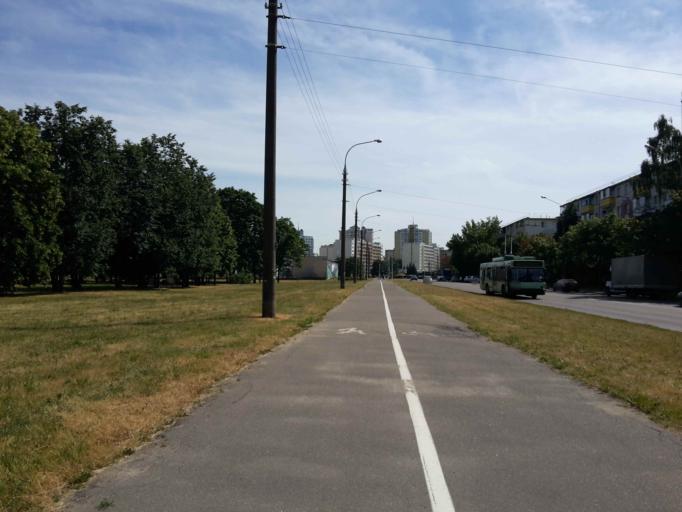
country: BY
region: Minsk
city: Minsk
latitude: 53.9312
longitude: 27.5659
